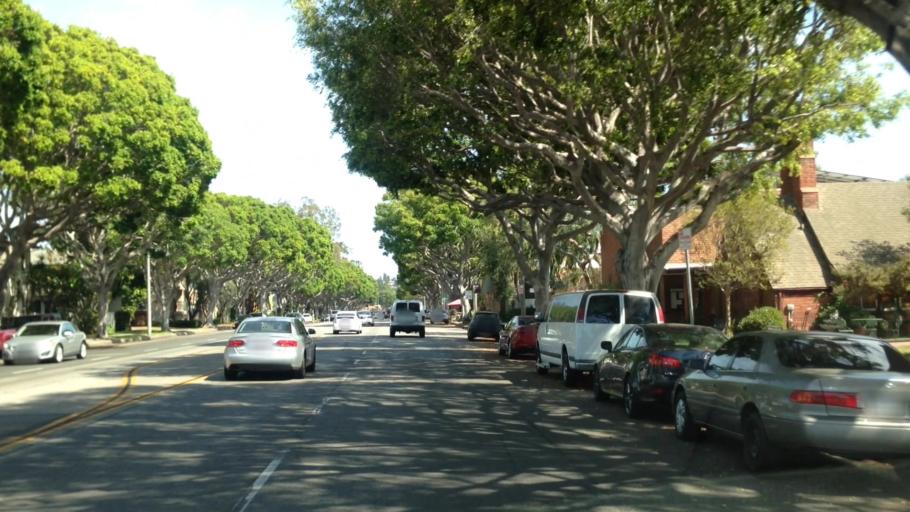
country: US
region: California
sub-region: Los Angeles County
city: Culver City
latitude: 34.0102
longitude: -118.3991
